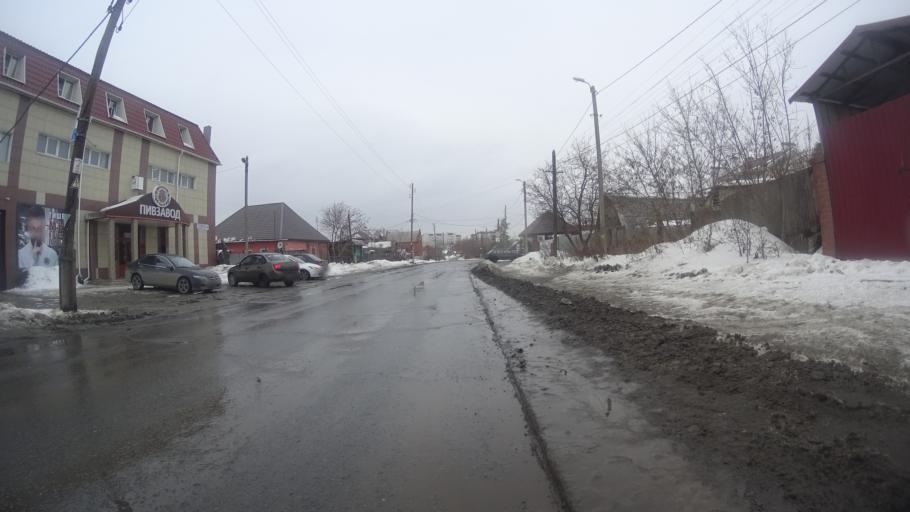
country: RU
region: Chelyabinsk
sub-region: Gorod Chelyabinsk
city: Chelyabinsk
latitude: 55.1302
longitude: 61.3951
